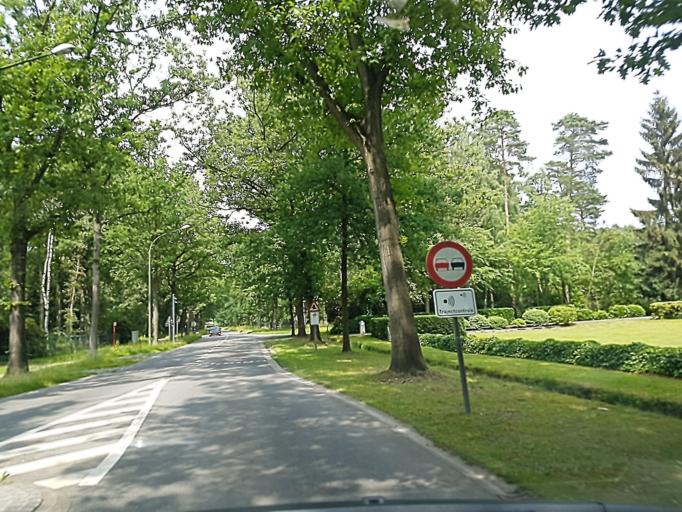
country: BE
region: Flanders
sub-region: Provincie Antwerpen
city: Wijnegem
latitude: 51.2427
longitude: 4.5393
